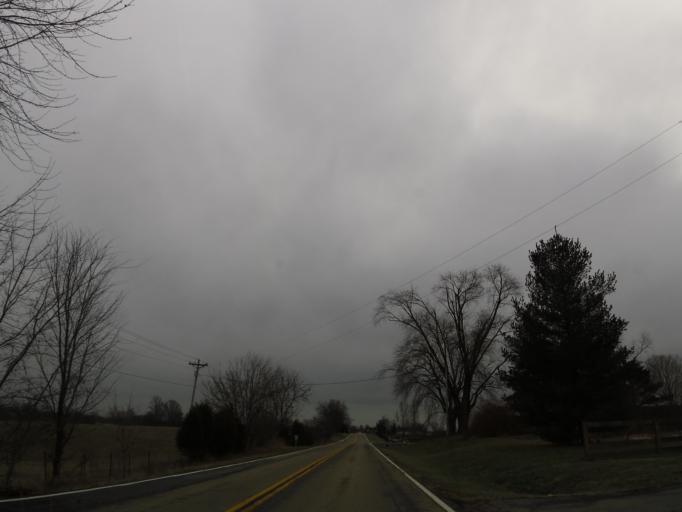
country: US
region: Kentucky
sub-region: Trimble County
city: Providence
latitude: 38.5363
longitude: -85.2580
